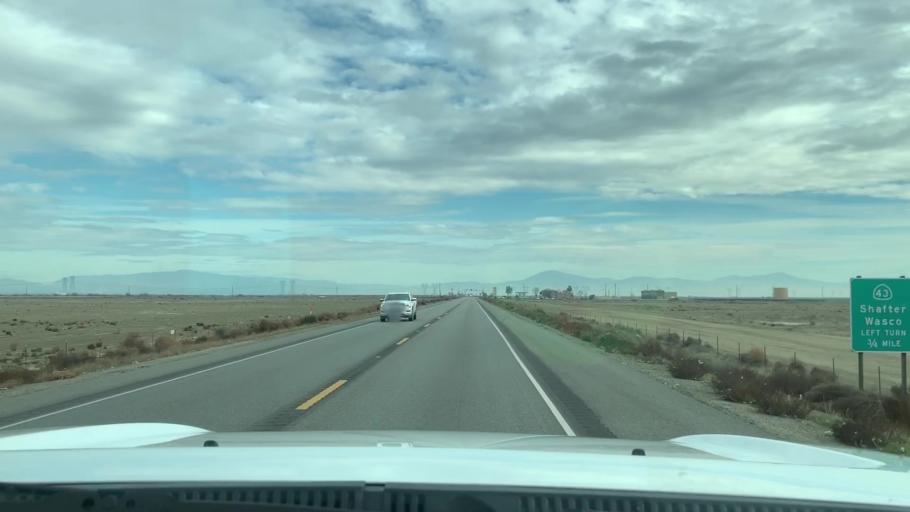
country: US
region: California
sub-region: Kern County
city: Rosedale
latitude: 35.2671
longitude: -119.2609
